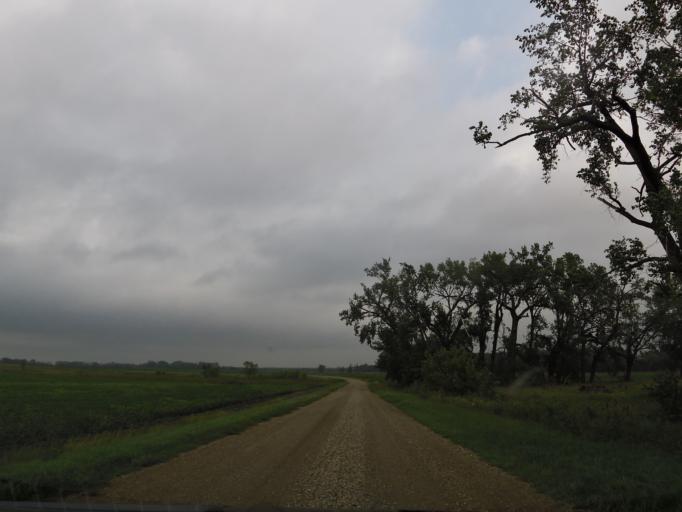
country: US
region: North Dakota
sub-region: Walsh County
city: Grafton
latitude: 48.4523
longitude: -97.1690
